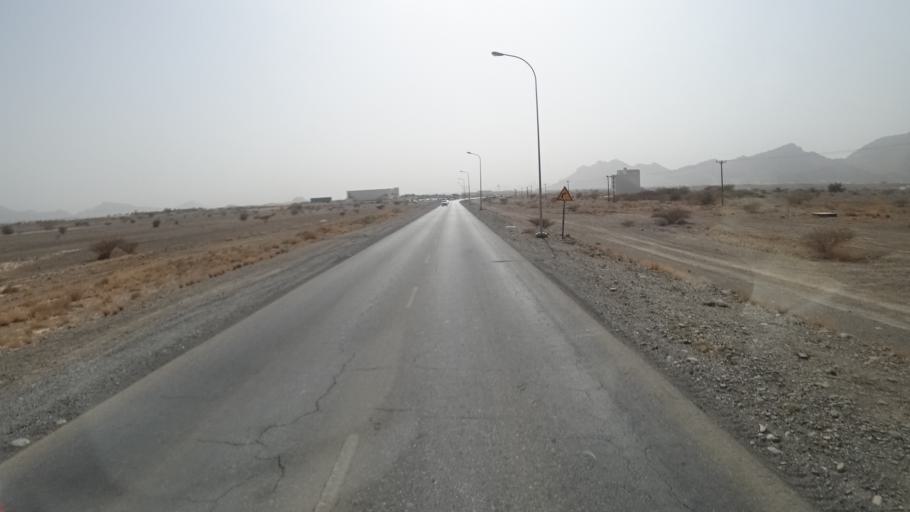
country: OM
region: Muhafazat ad Dakhiliyah
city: Nizwa
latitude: 22.9190
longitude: 57.6131
